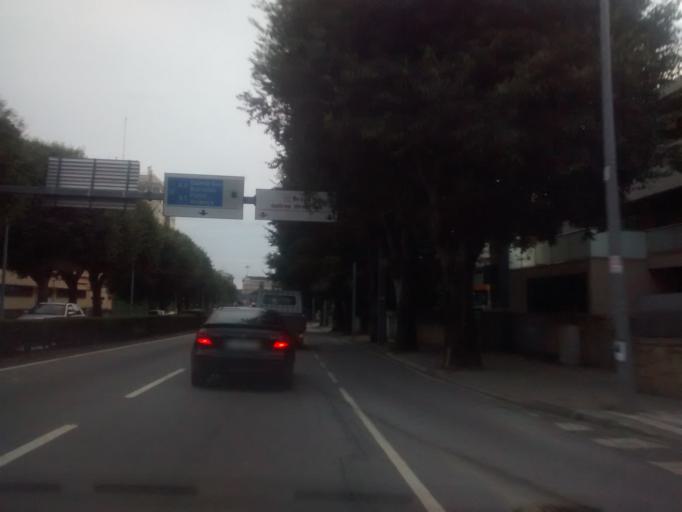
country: PT
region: Braga
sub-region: Braga
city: Braga
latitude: 41.5438
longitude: -8.4282
